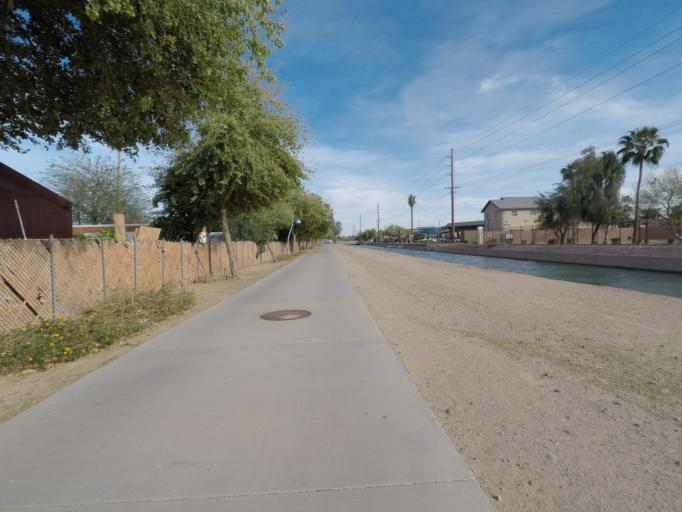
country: US
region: Arizona
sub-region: Maricopa County
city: Guadalupe
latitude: 33.3797
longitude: -111.9466
